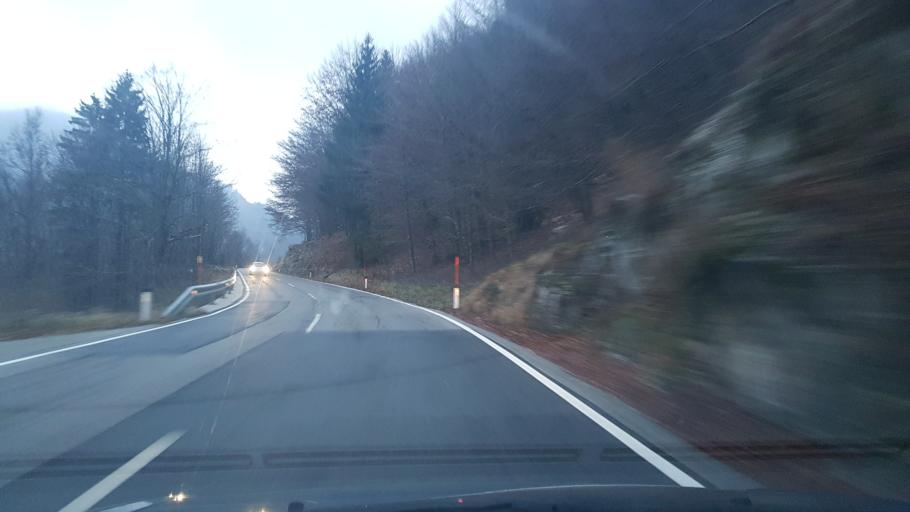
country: SI
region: Idrija
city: Idrija
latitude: 45.9146
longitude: 14.0327
